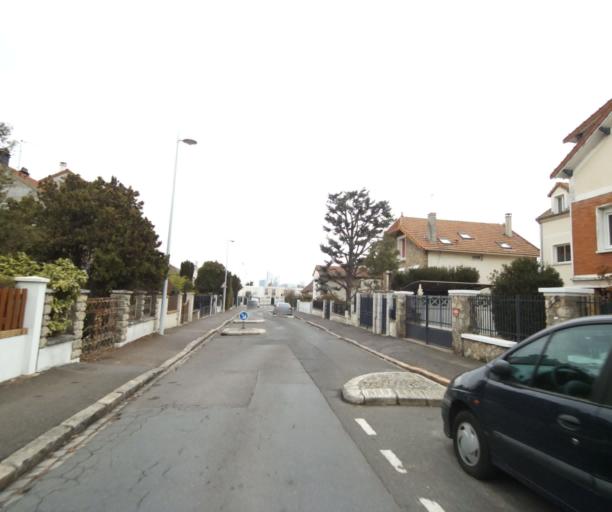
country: FR
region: Ile-de-France
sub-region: Departement des Hauts-de-Seine
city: Rueil-Malmaison
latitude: 48.8801
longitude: 2.2016
